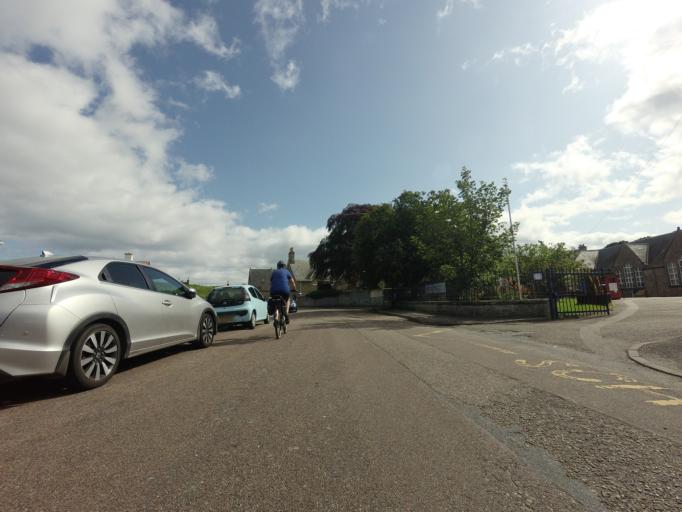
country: GB
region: Scotland
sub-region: Highland
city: Nairn
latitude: 57.5820
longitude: -3.8699
